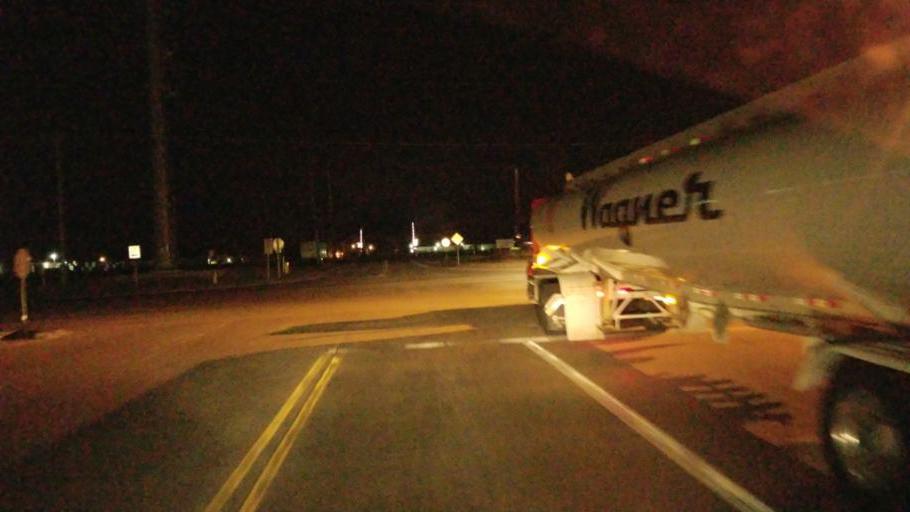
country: US
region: Wisconsin
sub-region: Fond du Lac County
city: Fond du Lac
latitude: 43.7479
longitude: -88.4626
